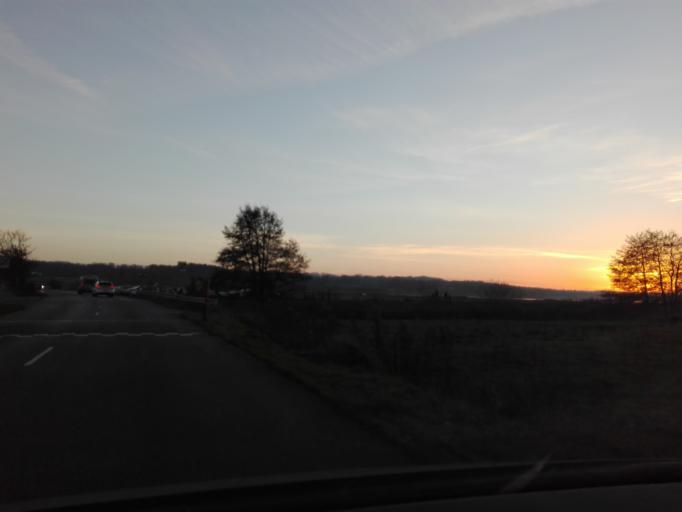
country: DK
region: Central Jutland
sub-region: Arhus Kommune
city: Stavtrup
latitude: 56.1483
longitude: 10.0886
